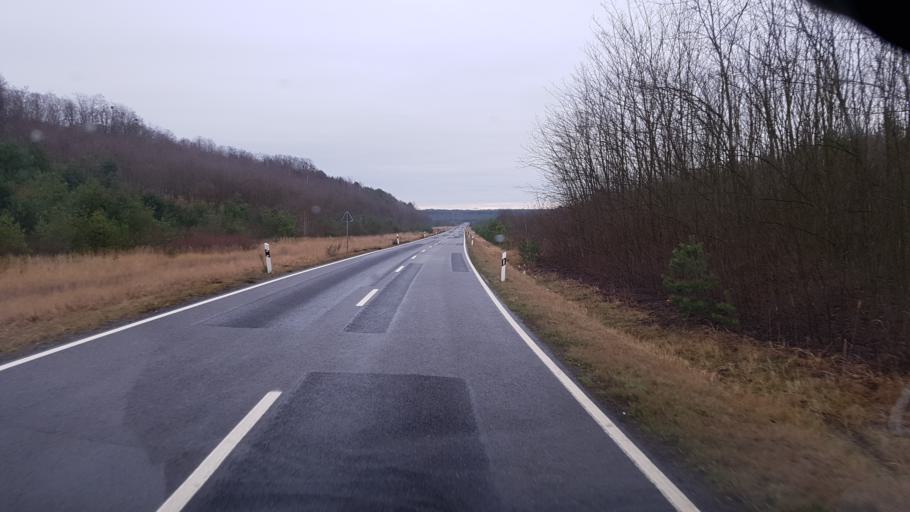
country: DE
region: Brandenburg
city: Schipkau
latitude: 51.5109
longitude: 13.8501
